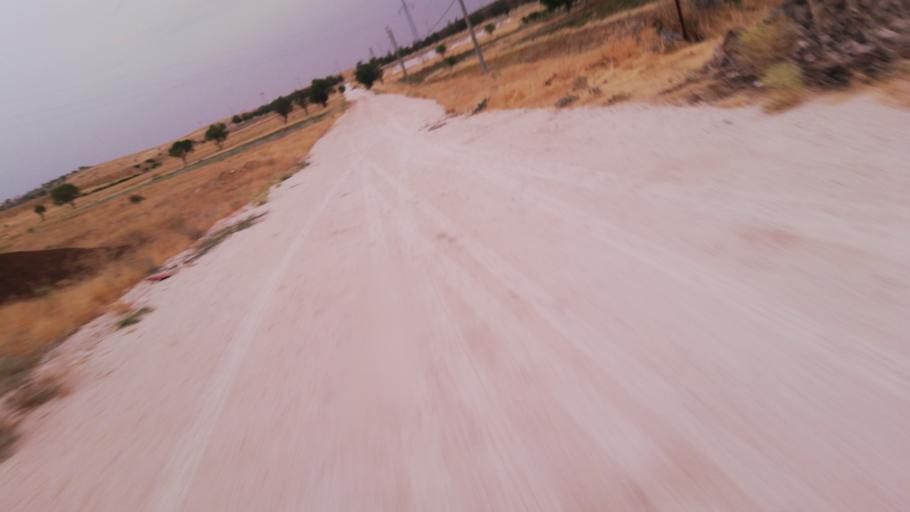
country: TR
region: Mardin
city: Kindirip
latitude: 37.4610
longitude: 41.2214
